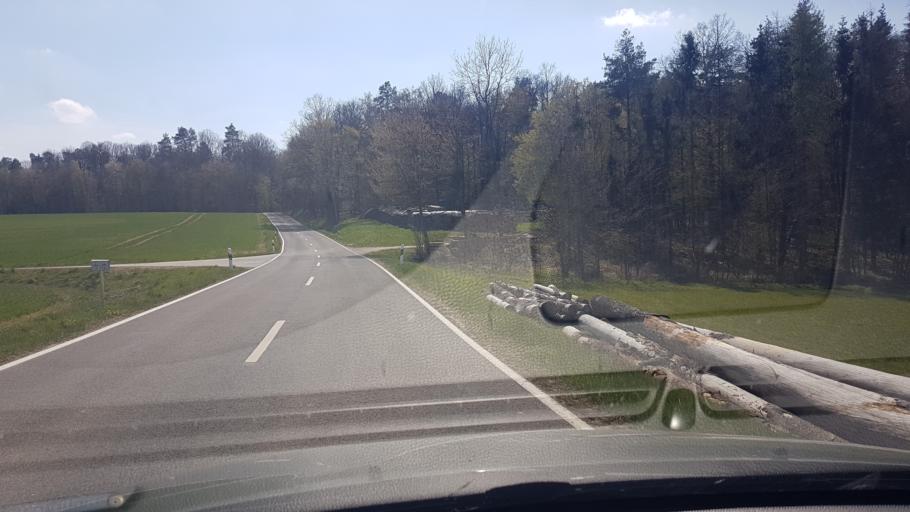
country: DE
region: Bavaria
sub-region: Upper Franconia
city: Zapfendorf
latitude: 50.0094
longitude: 10.9769
